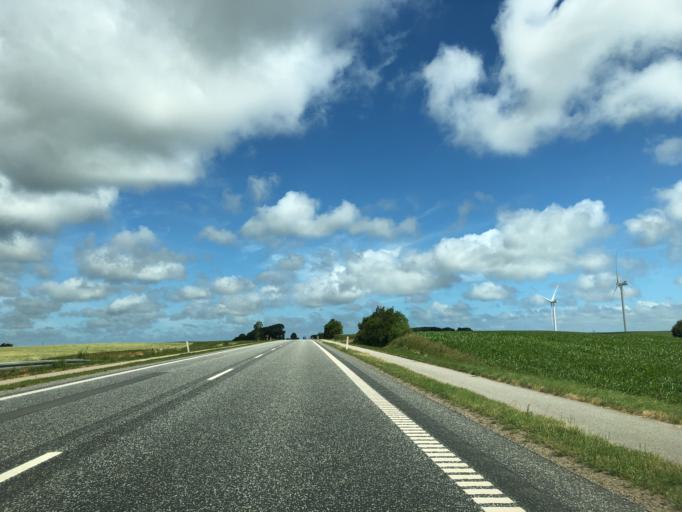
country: DK
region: Central Jutland
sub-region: Holstebro Kommune
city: Holstebro
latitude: 56.4177
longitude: 8.6020
